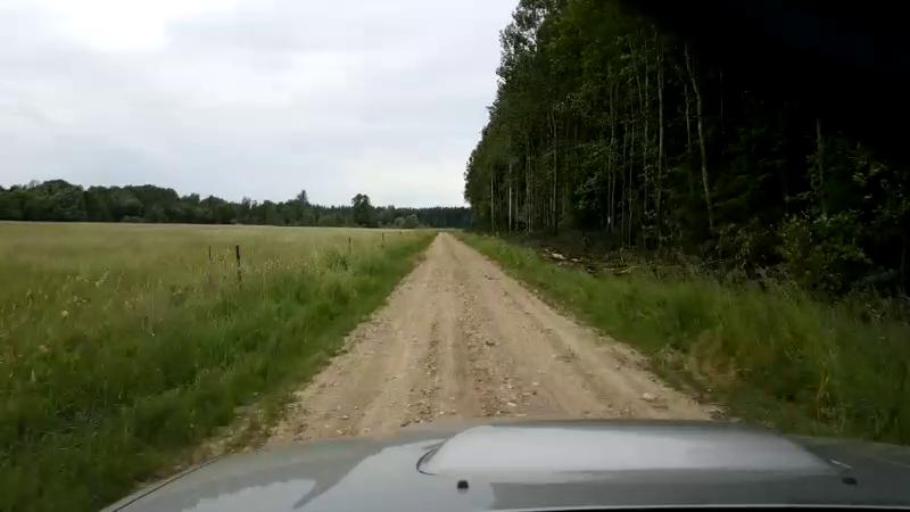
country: EE
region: Paernumaa
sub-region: Sindi linn
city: Sindi
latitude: 58.5104
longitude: 24.6210
